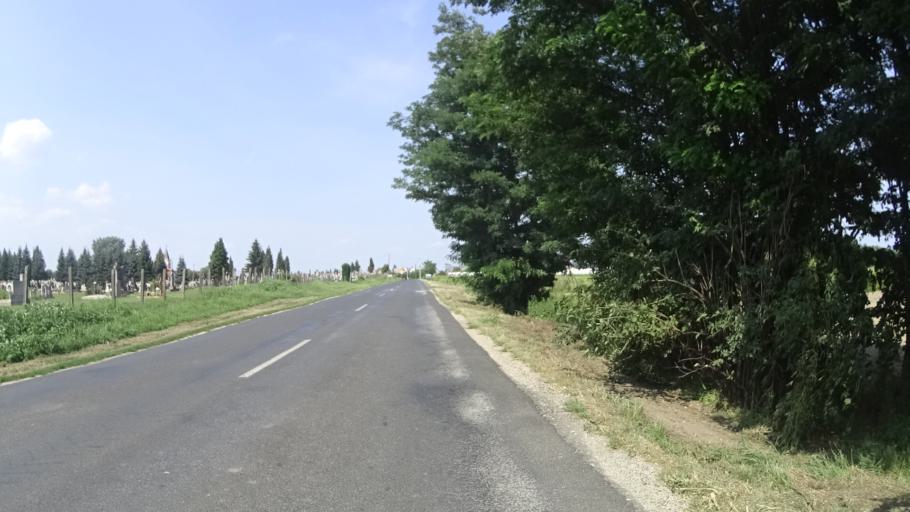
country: HU
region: Zala
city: Nagykanizsa
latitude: 46.4446
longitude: 16.9550
